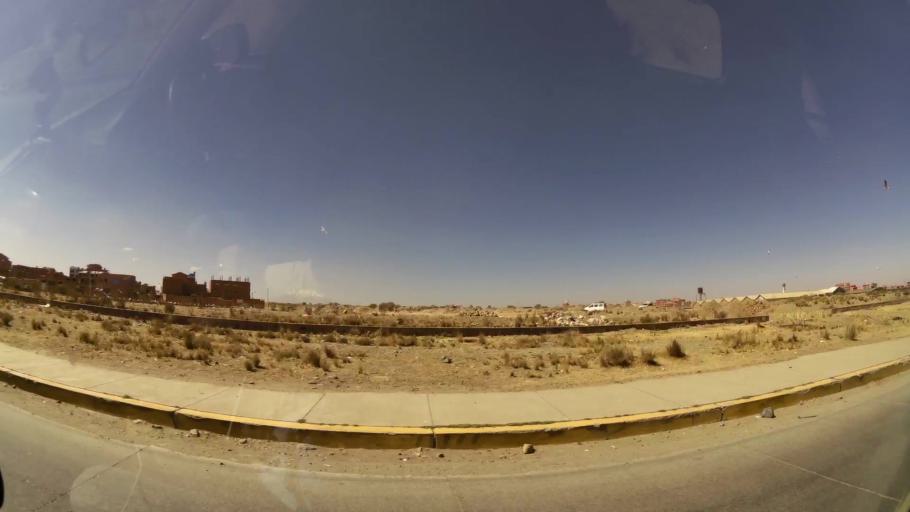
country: BO
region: La Paz
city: La Paz
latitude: -16.5095
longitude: -68.2132
